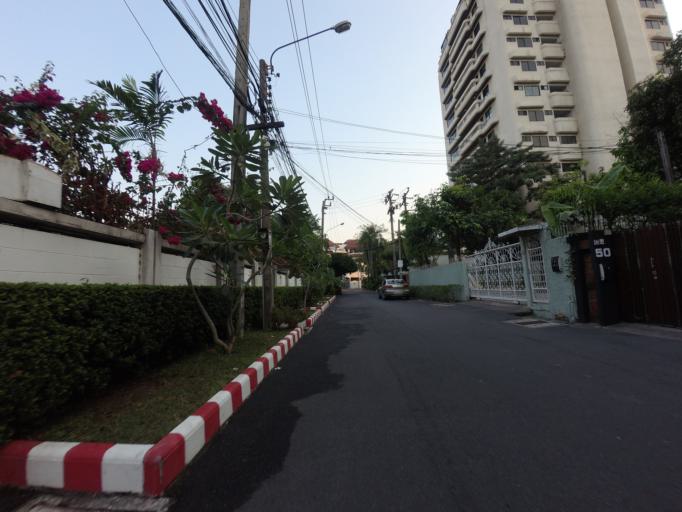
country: TH
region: Bangkok
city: Watthana
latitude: 13.7245
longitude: 100.5884
